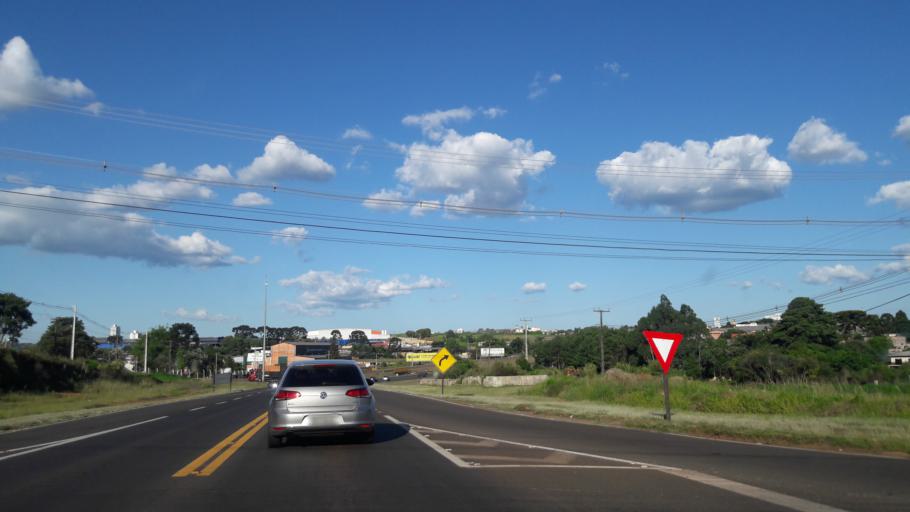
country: BR
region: Parana
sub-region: Guarapuava
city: Guarapuava
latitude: -25.3674
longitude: -51.4935
